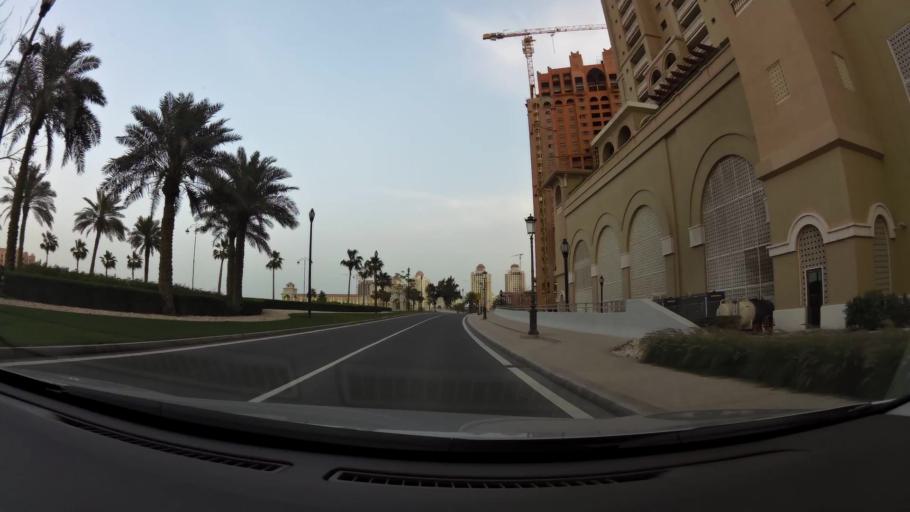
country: QA
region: Baladiyat ad Dawhah
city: Doha
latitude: 25.3738
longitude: 51.5467
